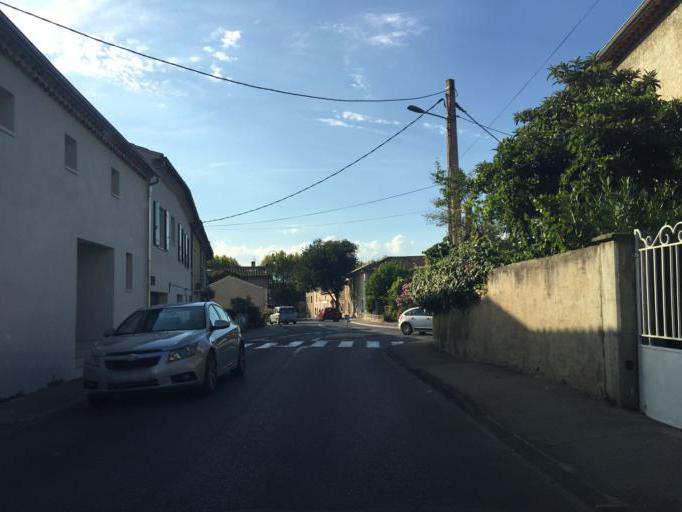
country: FR
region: Provence-Alpes-Cote d'Azur
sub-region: Departement du Vaucluse
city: Pernes-les-Fontaines
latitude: 43.9963
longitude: 5.0636
